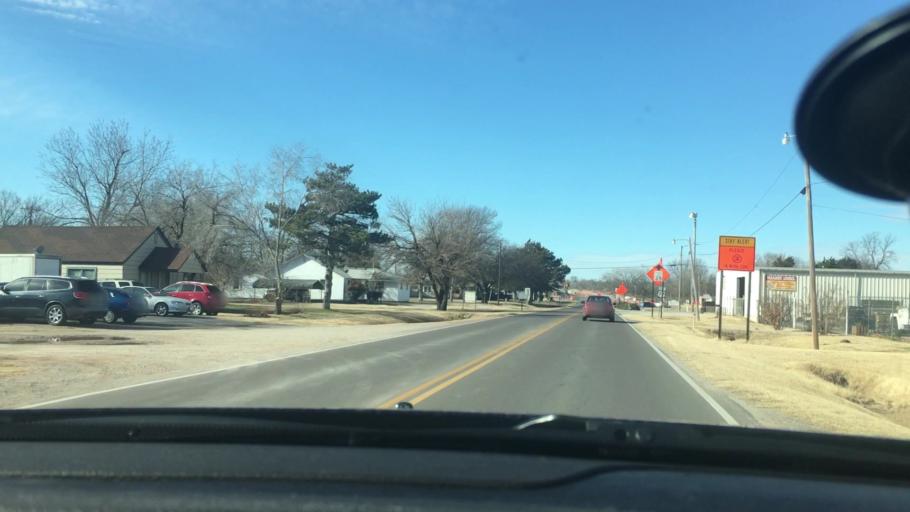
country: US
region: Oklahoma
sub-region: Cleveland County
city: Lexington
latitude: 35.0154
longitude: -97.3407
